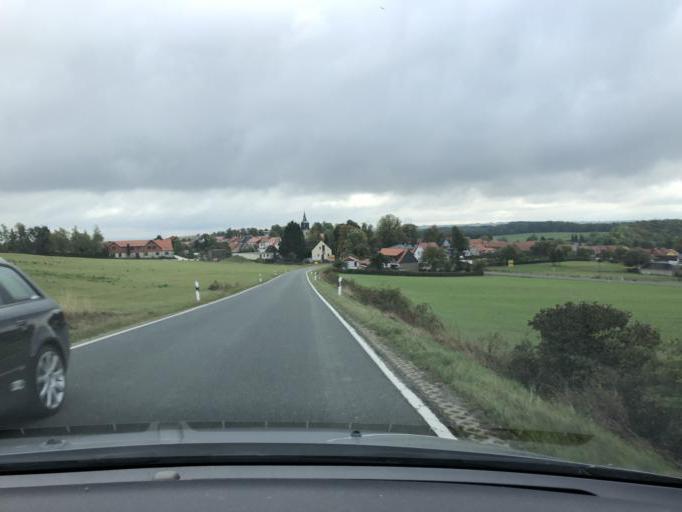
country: DE
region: Thuringia
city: Wachstedt
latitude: 51.2967
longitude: 10.2451
